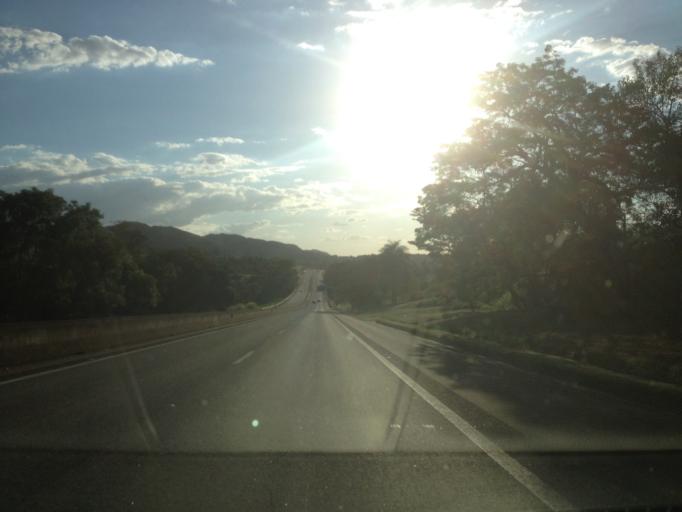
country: BR
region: Sao Paulo
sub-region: Brotas
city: Brotas
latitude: -22.2640
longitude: -48.2245
